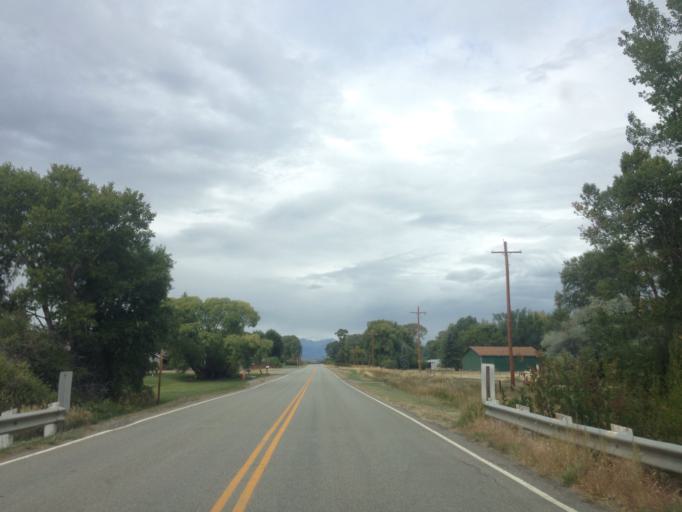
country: US
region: Montana
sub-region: Sweet Grass County
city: Big Timber
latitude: 45.7735
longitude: -109.8010
